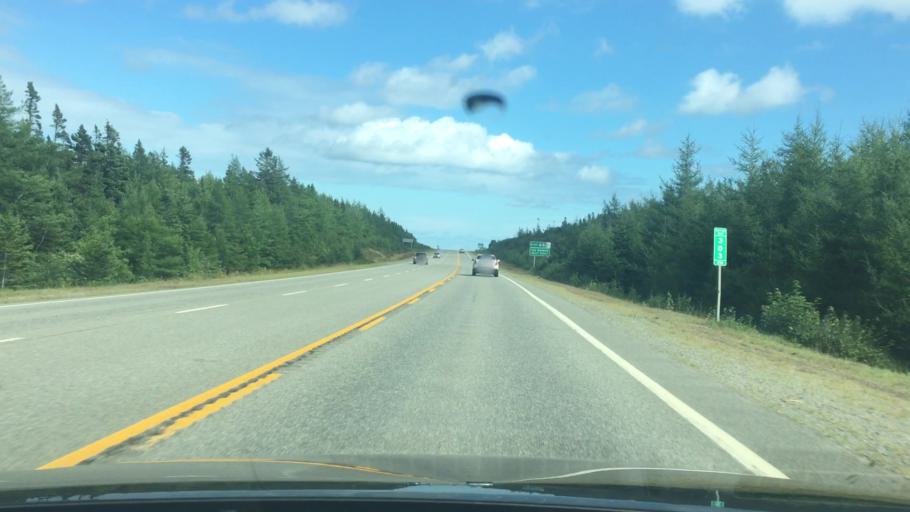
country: CA
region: Nova Scotia
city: Port Hawkesbury
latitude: 45.6155
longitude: -61.0978
